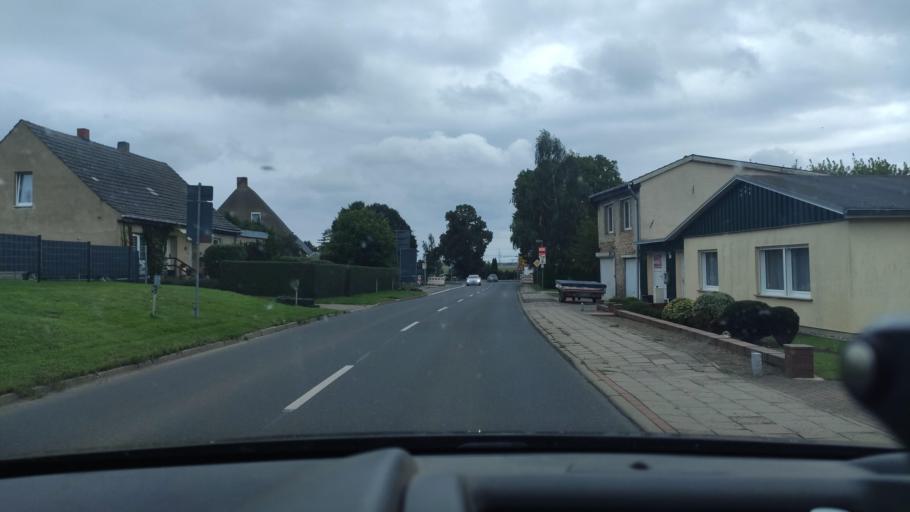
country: DE
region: Mecklenburg-Vorpommern
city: Guestrow
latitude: 53.8296
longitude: 12.1692
